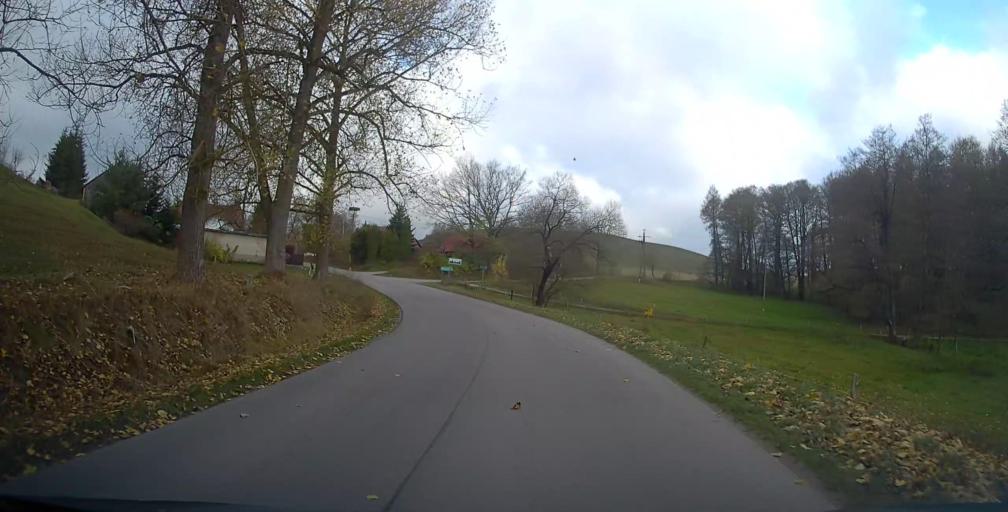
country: PL
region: Podlasie
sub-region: Suwalki
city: Suwalki
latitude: 54.2813
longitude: 22.9075
